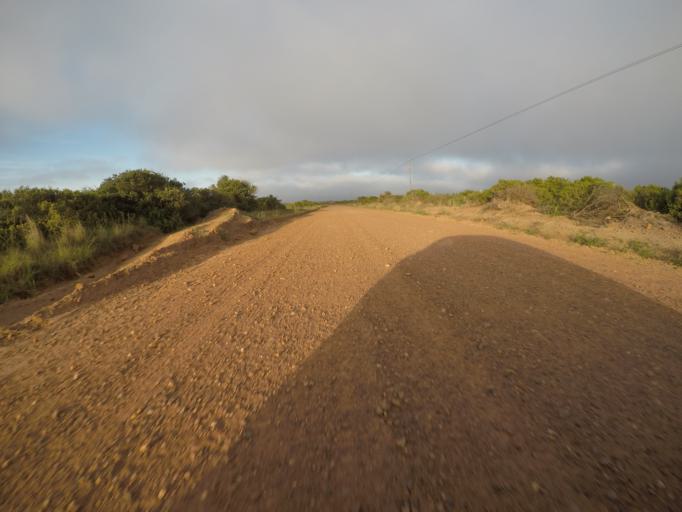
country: ZA
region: Western Cape
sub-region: Eden District Municipality
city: Mossel Bay
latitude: -34.1424
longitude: 22.0331
